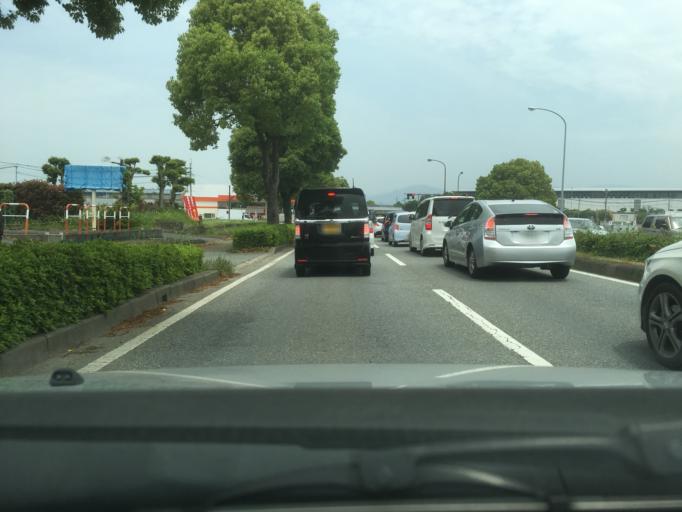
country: JP
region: Kumamoto
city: Kumamoto
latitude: 32.7934
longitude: 130.7870
